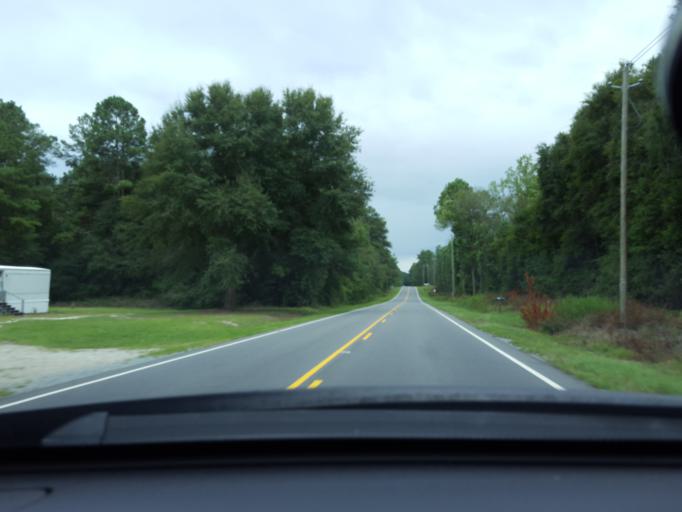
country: US
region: North Carolina
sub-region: Sampson County
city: Roseboro
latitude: 34.7771
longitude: -78.4000
